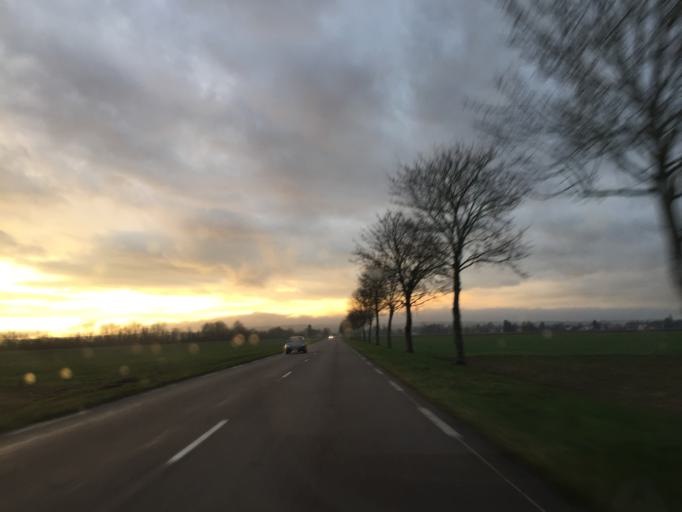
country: FR
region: Franche-Comte
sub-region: Departement du Jura
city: Choisey
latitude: 47.0348
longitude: 5.4953
